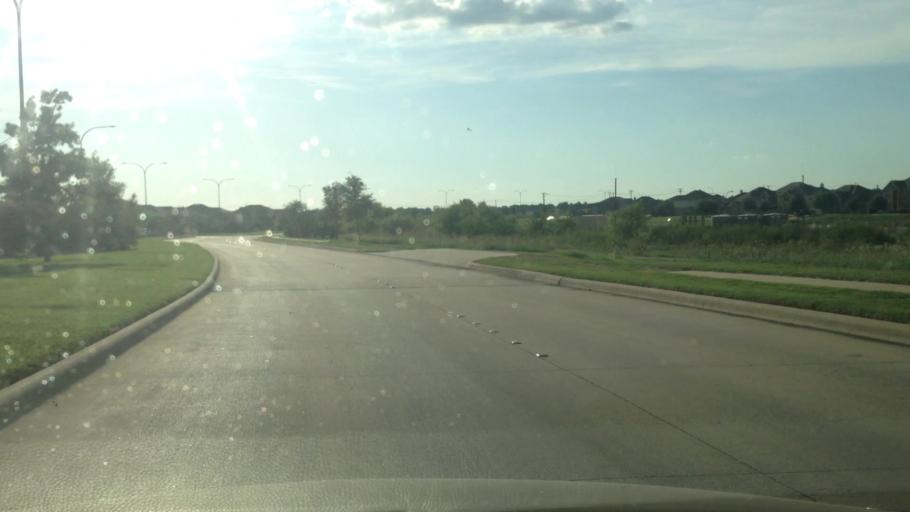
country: US
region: Texas
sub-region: Tarrant County
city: Haslet
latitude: 32.9892
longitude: -97.3920
